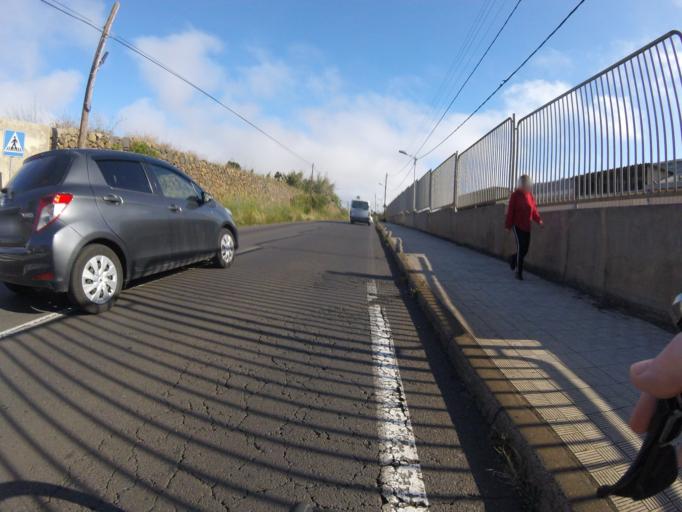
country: ES
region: Canary Islands
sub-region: Provincia de Santa Cruz de Tenerife
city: La Laguna
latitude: 28.4739
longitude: -16.3177
